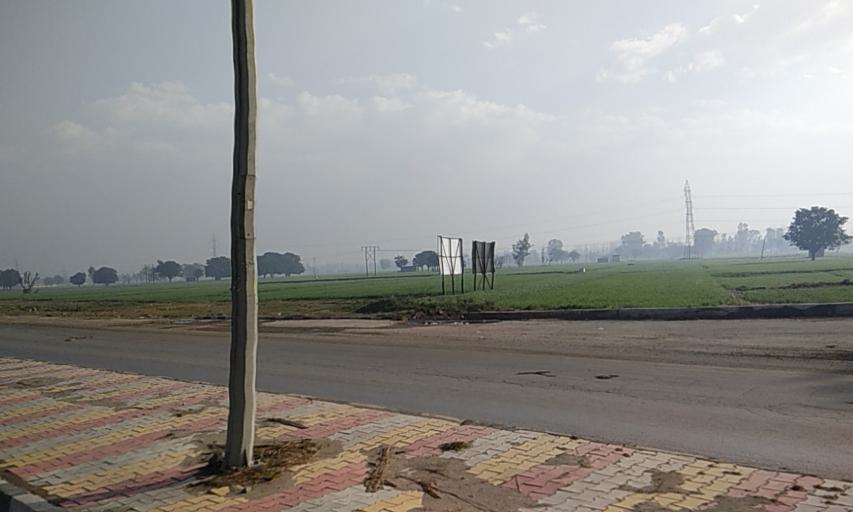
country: IN
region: Punjab
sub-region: Gurdaspur
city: Dinanagar
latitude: 32.1960
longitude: 75.5326
